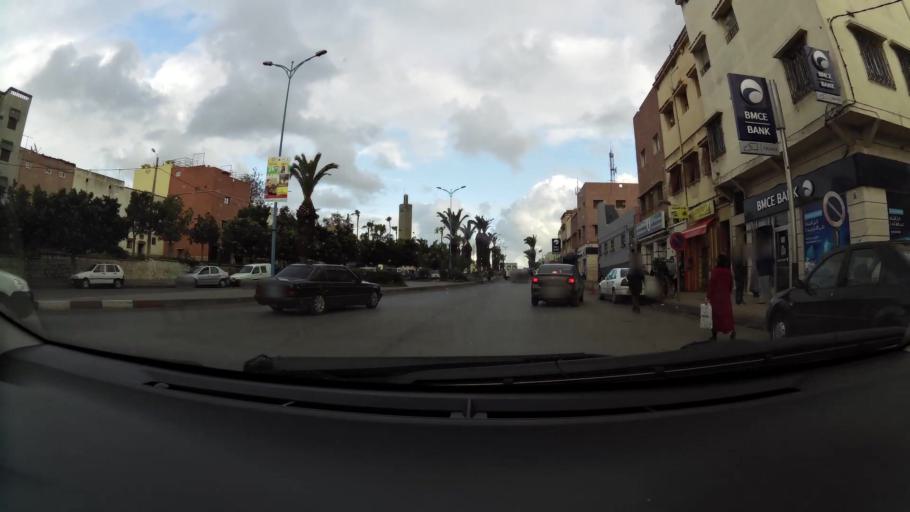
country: MA
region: Grand Casablanca
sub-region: Mohammedia
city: Mohammedia
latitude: 33.6880
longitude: -7.3919
